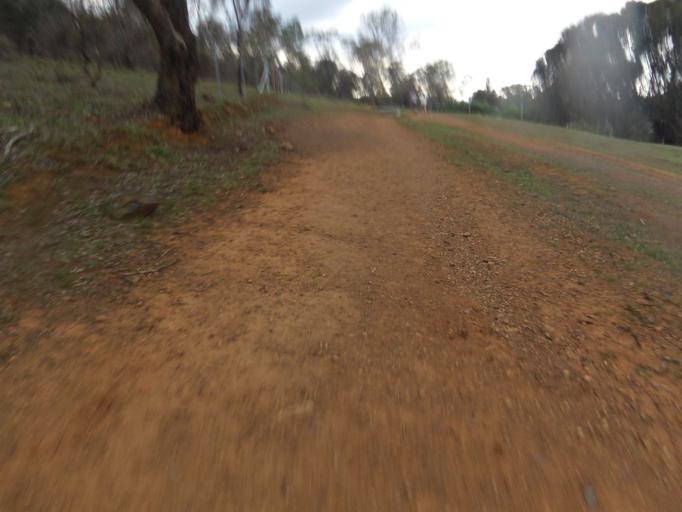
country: AU
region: Australian Capital Territory
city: Forrest
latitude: -35.3295
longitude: 149.1207
